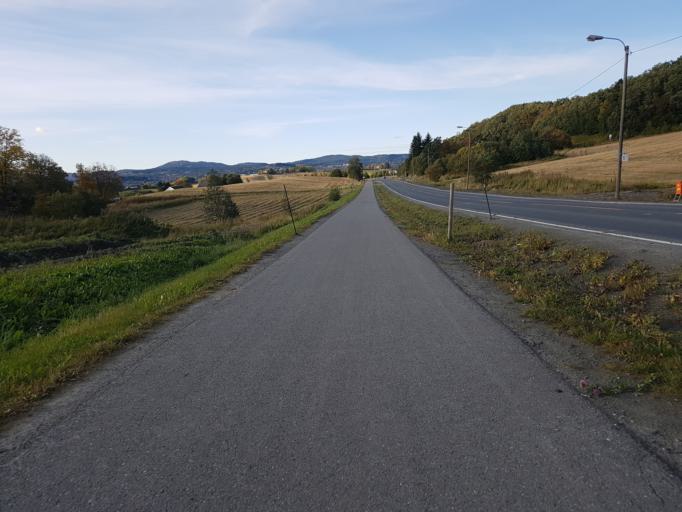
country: NO
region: Sor-Trondelag
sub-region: Trondheim
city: Trondheim
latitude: 63.3707
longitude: 10.4358
